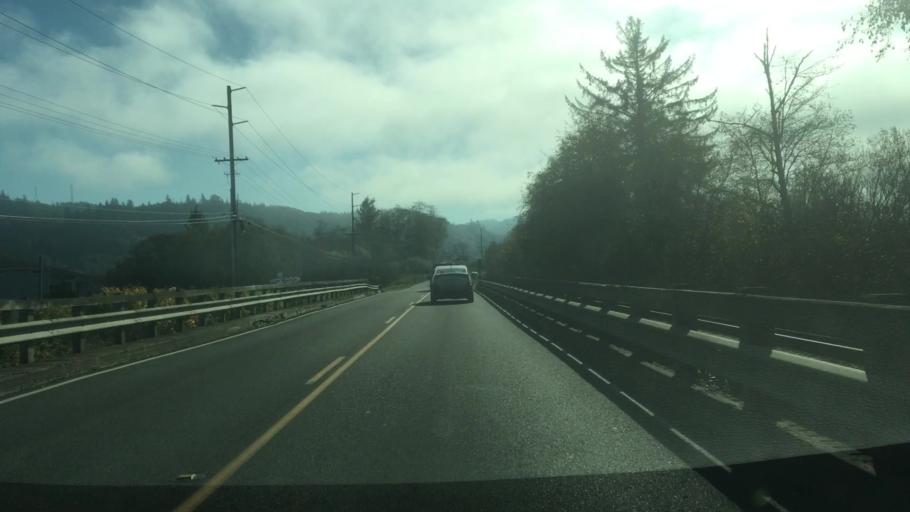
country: US
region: Washington
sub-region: Grays Harbor County
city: Montesano
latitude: 46.9736
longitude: -123.6010
